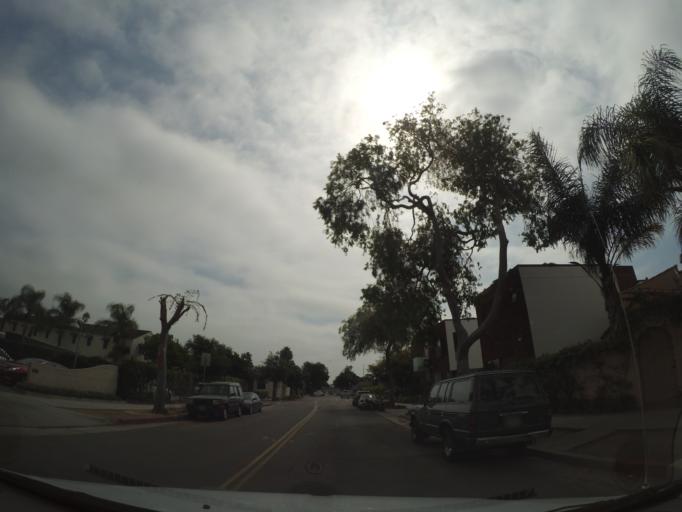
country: US
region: California
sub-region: Santa Barbara County
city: Santa Barbara
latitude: 34.4207
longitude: -119.6930
